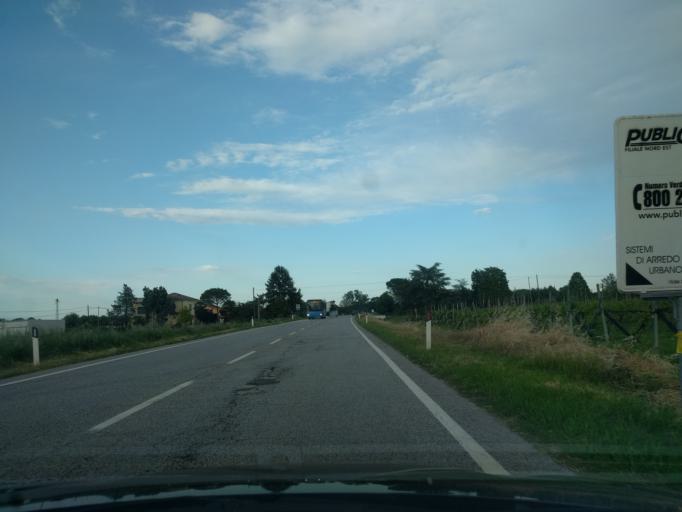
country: IT
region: Veneto
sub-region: Provincia di Rovigo
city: Canaro
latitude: 44.9296
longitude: 11.7110
